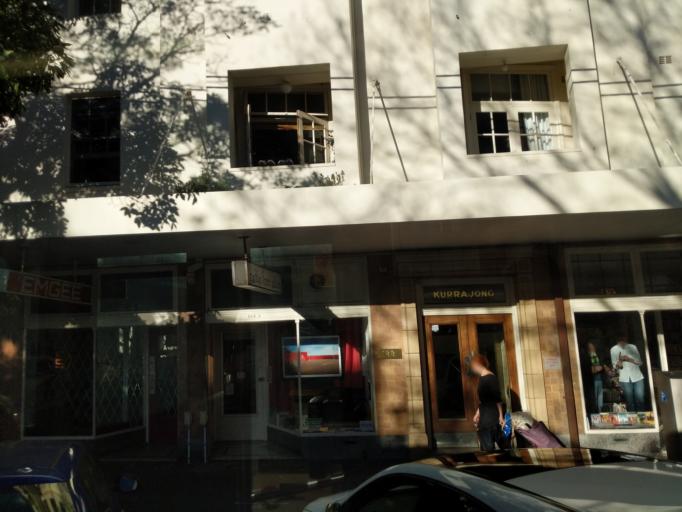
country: AU
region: New South Wales
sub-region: City of Sydney
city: Darlinghurst
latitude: -33.8786
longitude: 151.2202
